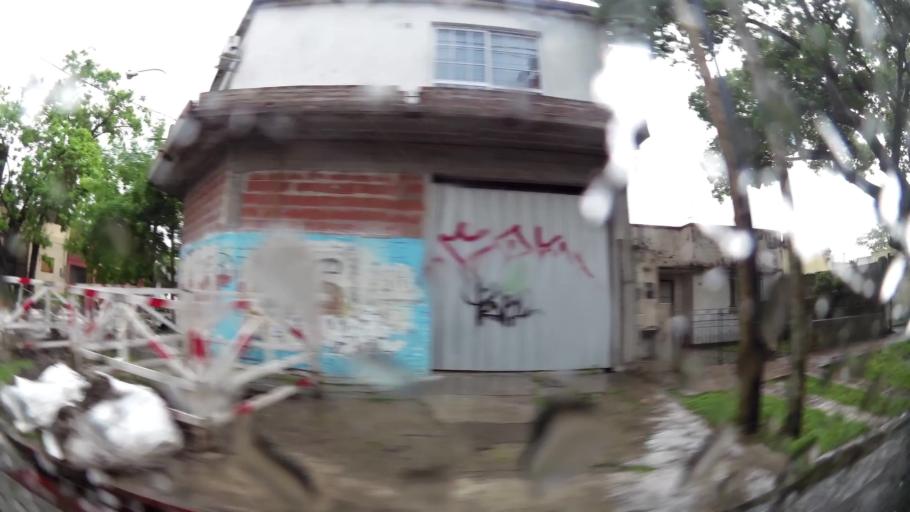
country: AR
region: Buenos Aires
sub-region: Partido de Lanus
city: Lanus
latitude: -34.7148
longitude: -58.4084
